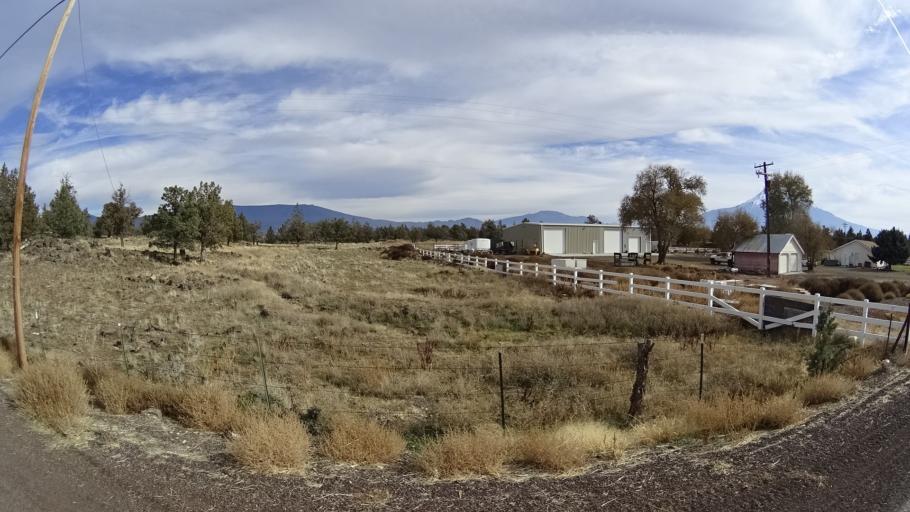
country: US
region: California
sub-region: Siskiyou County
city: Montague
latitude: 41.6113
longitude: -122.4000
